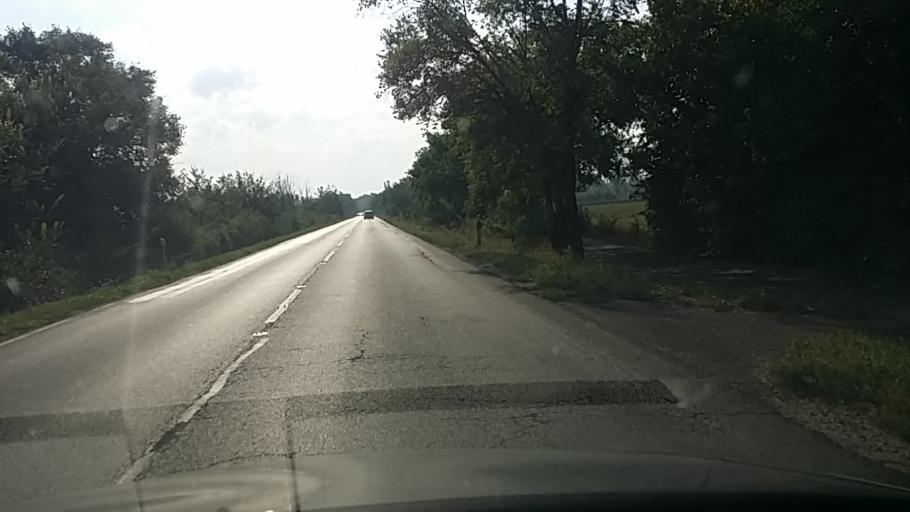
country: HU
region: Bekes
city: Bekesszentandras
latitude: 46.8691
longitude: 20.5136
